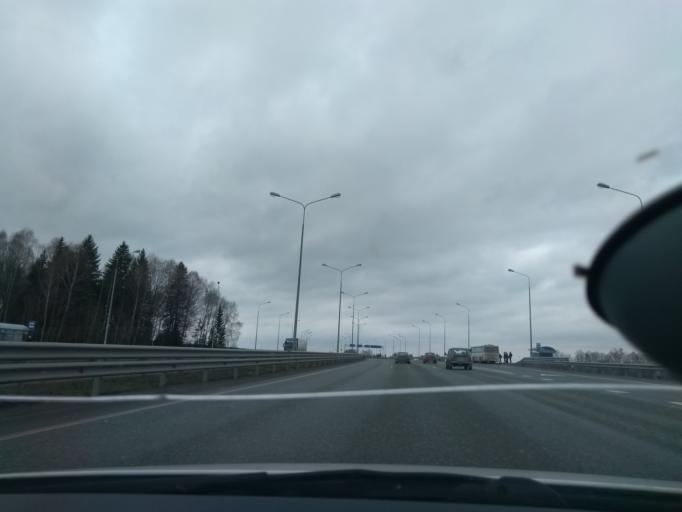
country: RU
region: Perm
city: Bershet'
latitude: 57.6809
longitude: 56.4281
